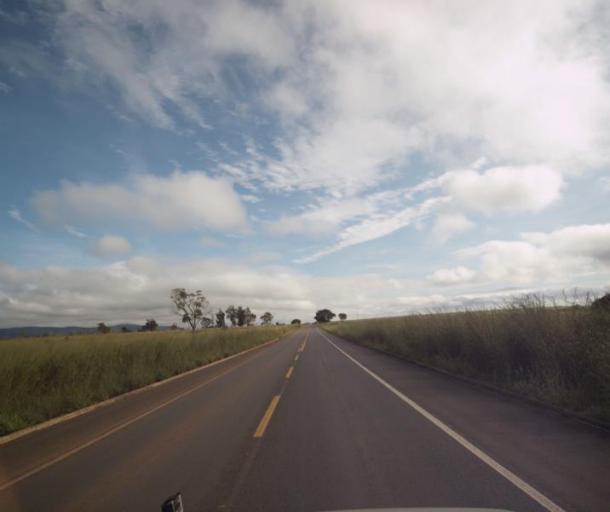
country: BR
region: Goias
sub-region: Padre Bernardo
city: Padre Bernardo
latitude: -15.4473
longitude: -48.6171
